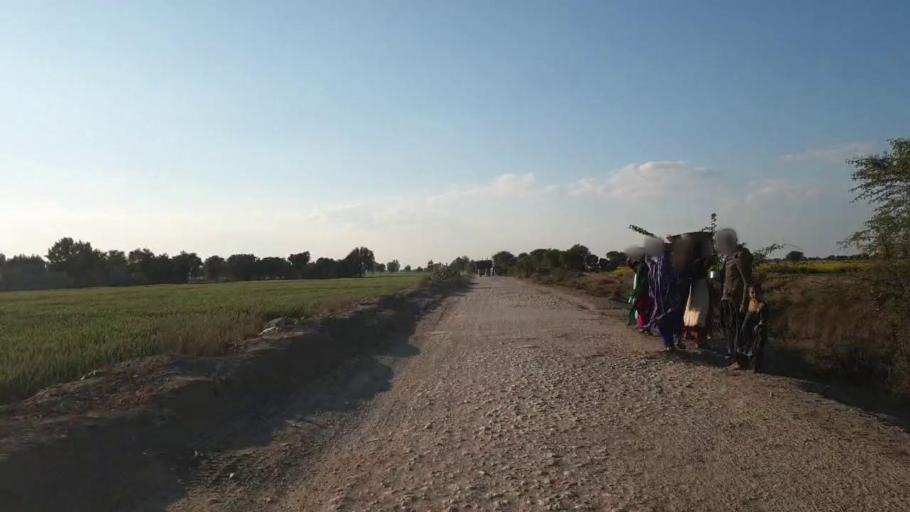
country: PK
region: Sindh
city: Shahpur Chakar
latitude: 26.1362
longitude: 68.5599
